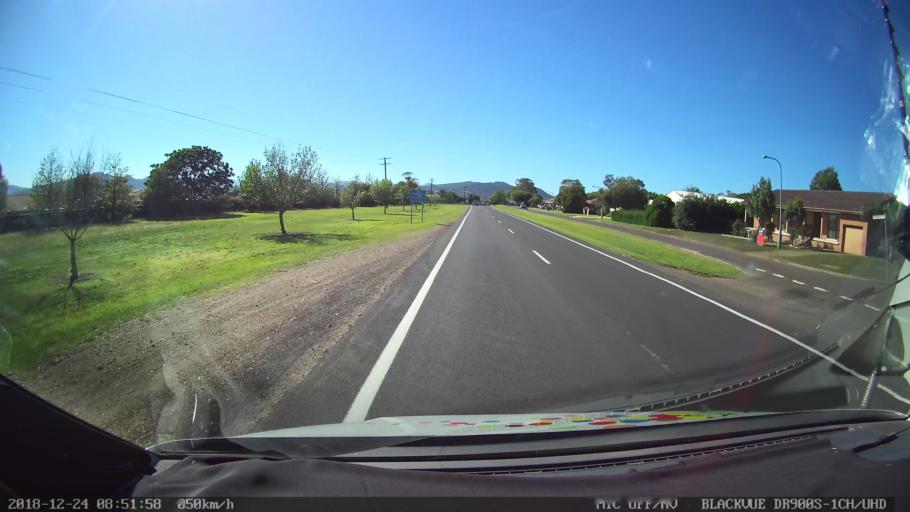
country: AU
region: New South Wales
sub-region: Liverpool Plains
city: Quirindi
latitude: -31.4886
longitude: 150.6771
